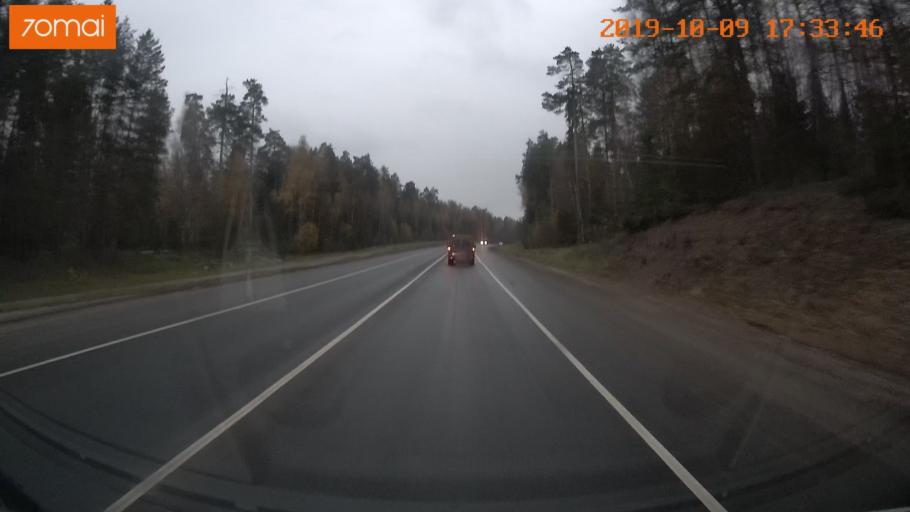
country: RU
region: Ivanovo
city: Bogorodskoye
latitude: 57.1137
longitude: 41.0177
